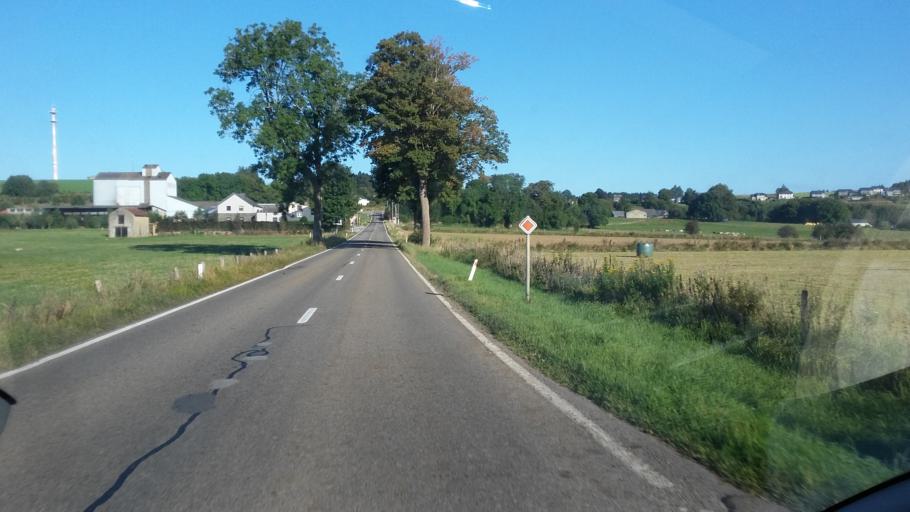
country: BE
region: Wallonia
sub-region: Province du Luxembourg
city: Neufchateau
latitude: 49.8281
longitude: 5.4843
